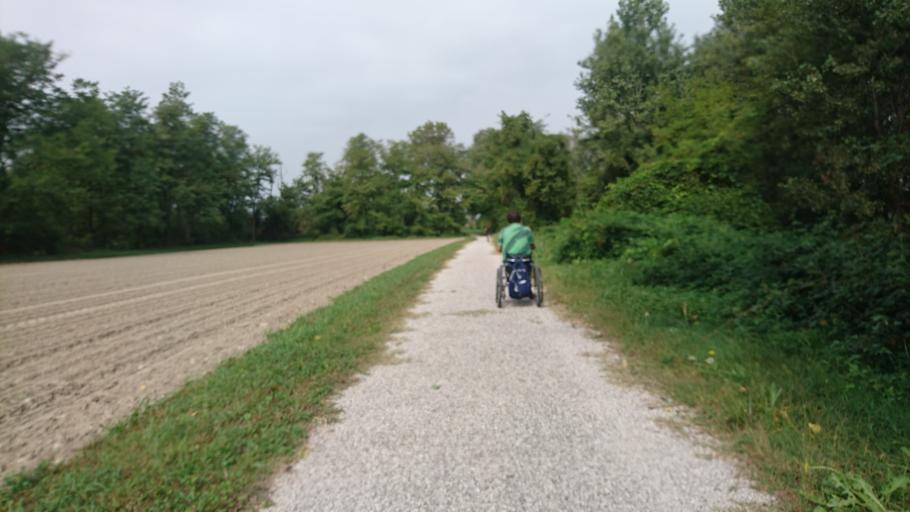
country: IT
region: Veneto
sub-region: Provincia di Padova
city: Grantorto
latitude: 45.5731
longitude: 11.7594
